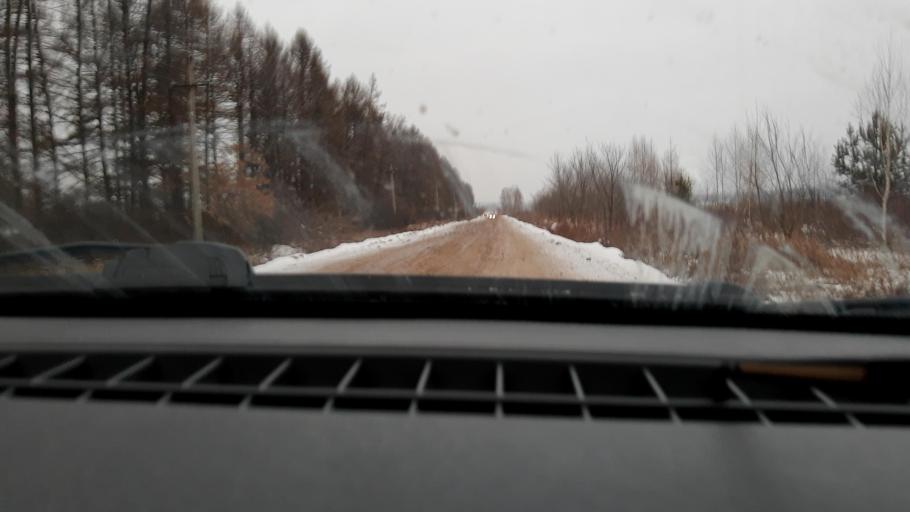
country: RU
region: Bashkortostan
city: Iglino
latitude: 54.7352
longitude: 56.2547
